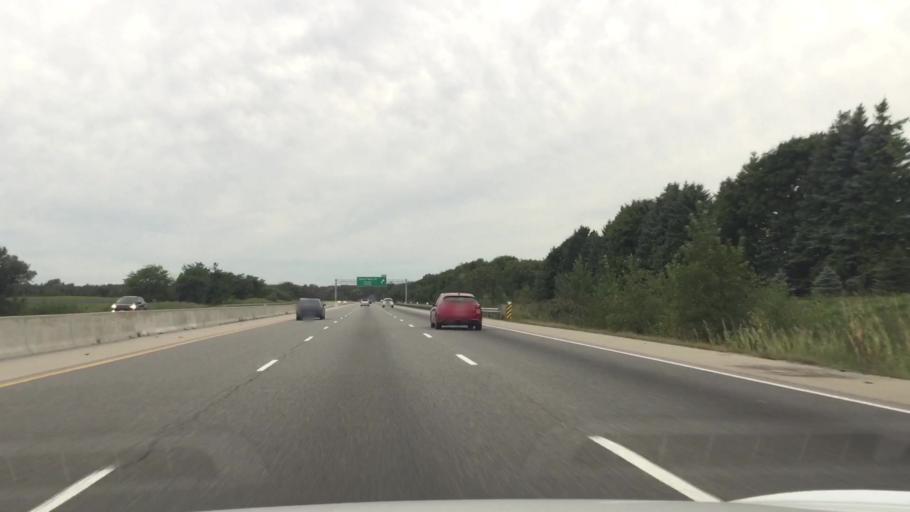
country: CA
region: Ontario
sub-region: Oxford County
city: Woodstock
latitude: 43.2370
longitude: -80.5867
